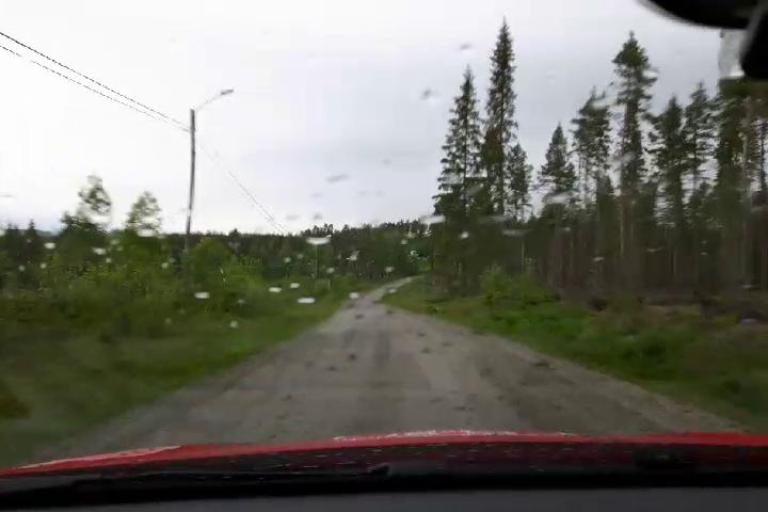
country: SE
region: Jaemtland
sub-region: Bergs Kommun
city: Hoverberg
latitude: 62.7462
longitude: 14.4525
